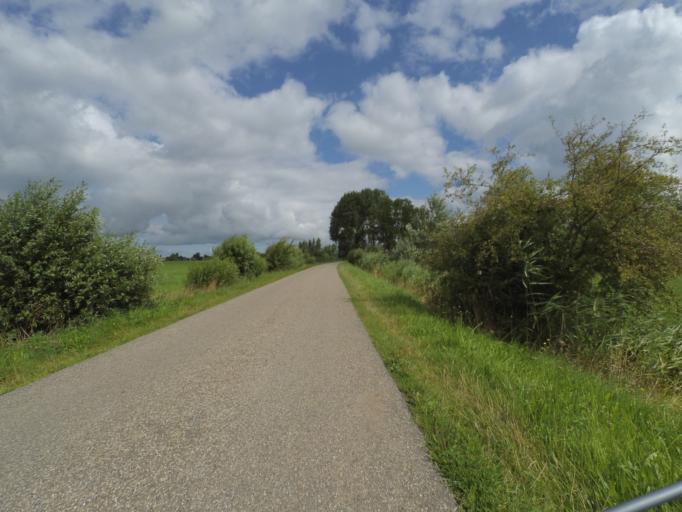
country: NL
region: Friesland
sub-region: Gemeente Kollumerland en Nieuwkruisland
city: Kollum
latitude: 53.2689
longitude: 6.1758
